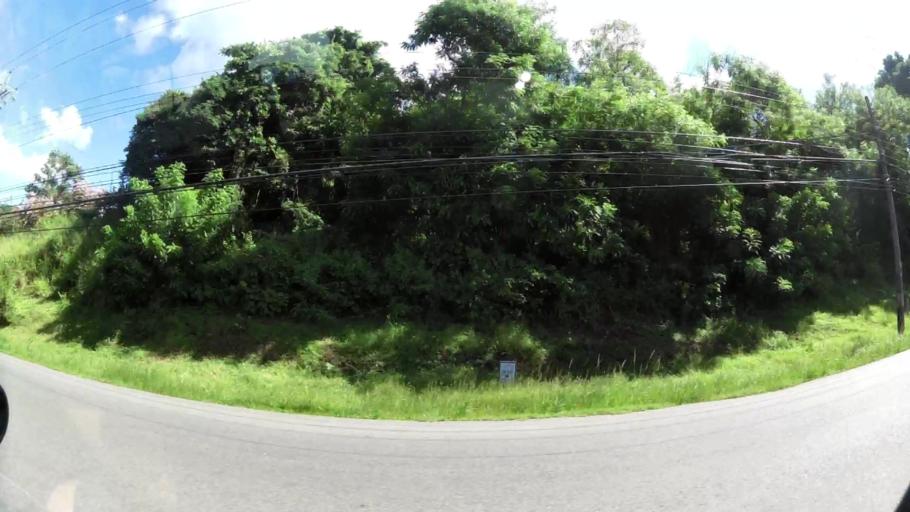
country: TT
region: Tobago
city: Scarborough
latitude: 11.2022
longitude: -60.7851
